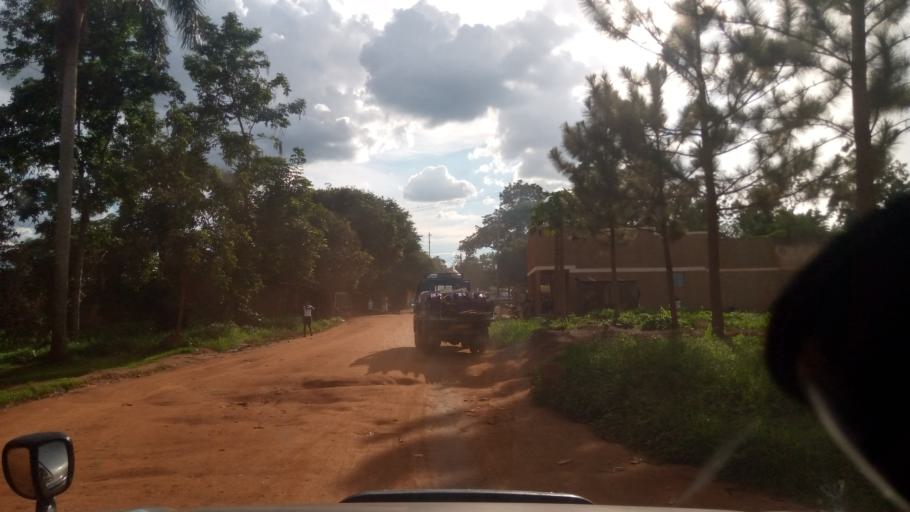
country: UG
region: Northern Region
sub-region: Lira District
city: Lira
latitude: 2.2275
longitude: 32.8966
